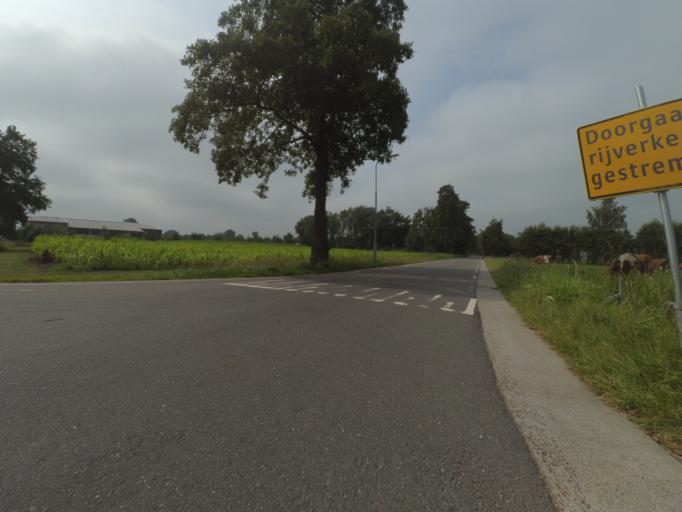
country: NL
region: Gelderland
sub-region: Gemeente Barneveld
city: Kootwijkerbroek
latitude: 52.1371
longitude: 5.6815
